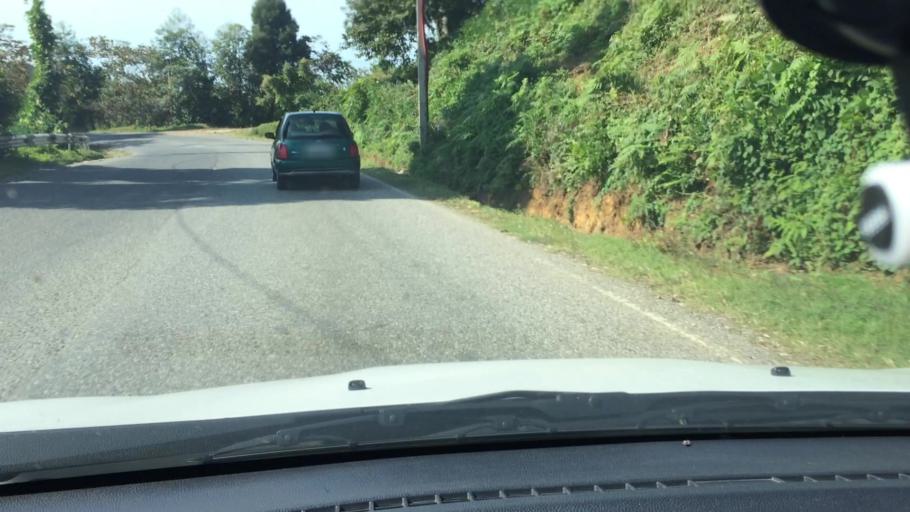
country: GE
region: Ajaria
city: Kobuleti
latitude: 41.7502
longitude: 41.7431
